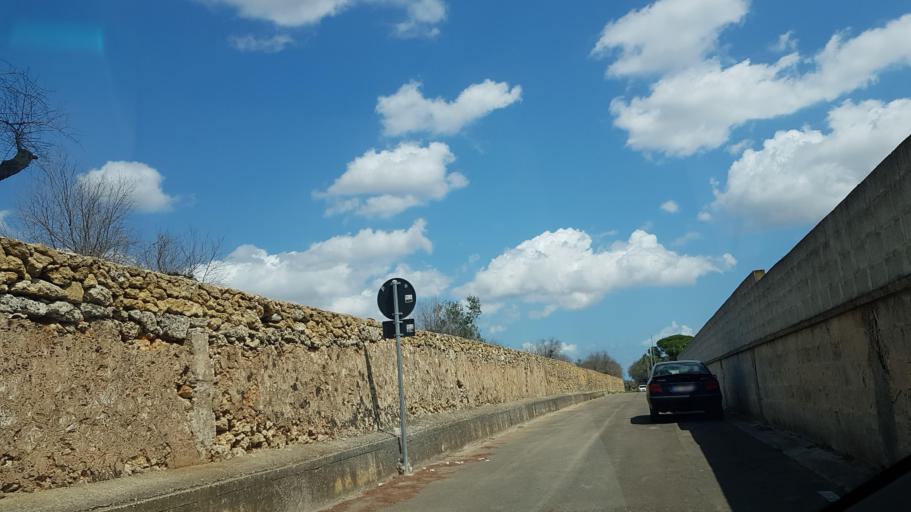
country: IT
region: Apulia
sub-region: Provincia di Lecce
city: Trepuzzi
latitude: 40.4081
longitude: 18.0588
